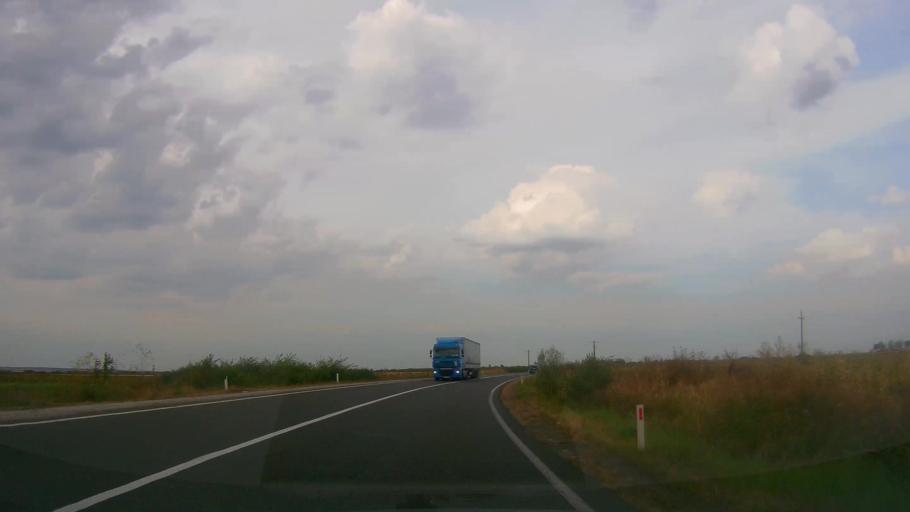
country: RO
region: Satu Mare
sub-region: Comuna Acas
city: Acas
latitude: 47.5388
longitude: 22.8044
